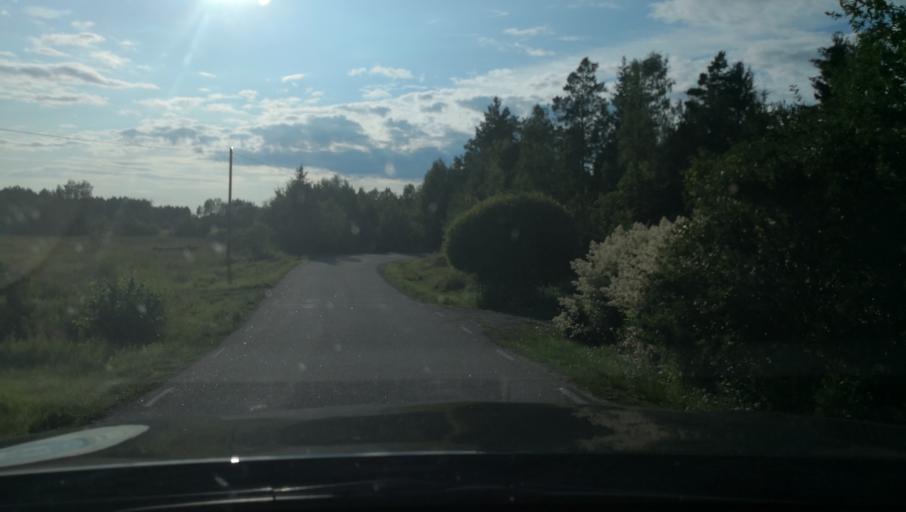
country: SE
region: Uppsala
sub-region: Osthammars Kommun
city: Osterbybruk
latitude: 60.0178
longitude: 17.9247
